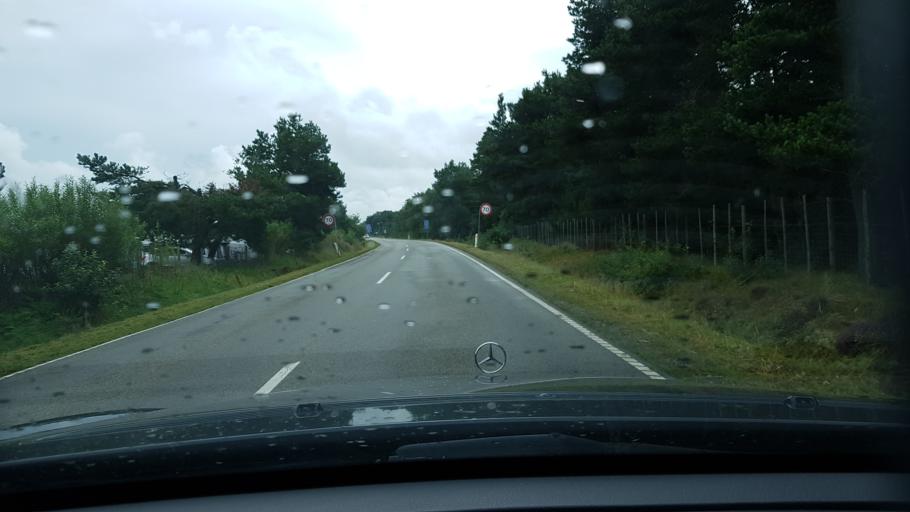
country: DK
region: North Denmark
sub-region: Alborg Kommune
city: Hals
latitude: 56.8236
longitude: 10.2691
